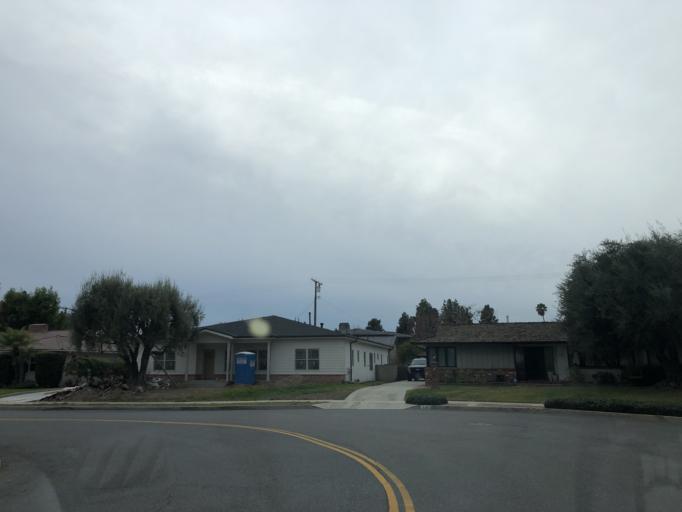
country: US
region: California
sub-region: Los Angeles County
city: San Marino
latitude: 34.1149
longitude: -118.0948
